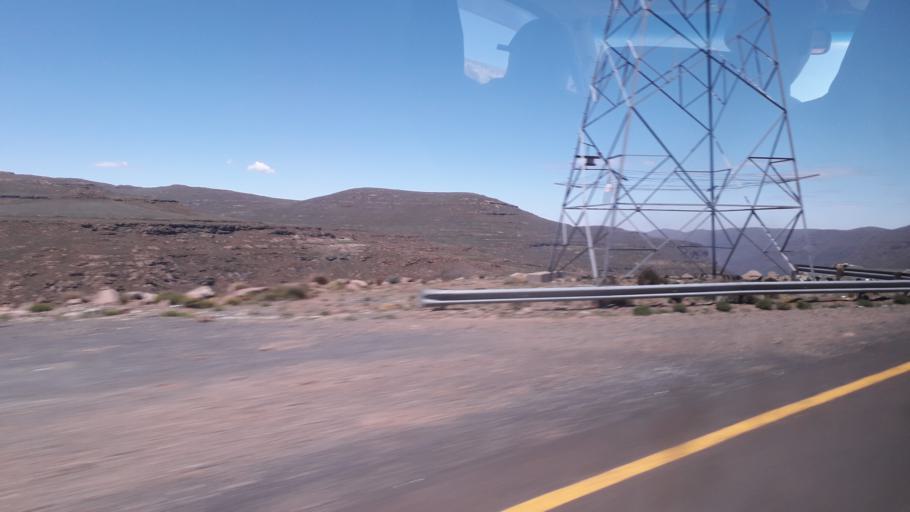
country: ZA
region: Orange Free State
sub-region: Thabo Mofutsanyana District Municipality
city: Phuthaditjhaba
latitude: -28.8301
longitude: 28.7327
